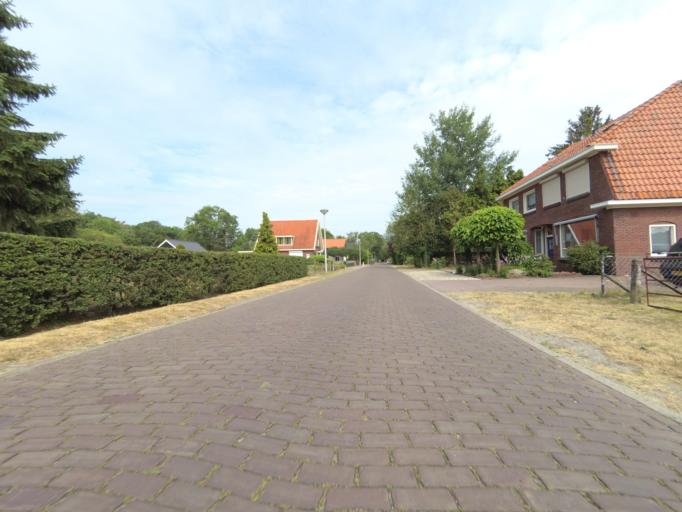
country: NL
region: Overijssel
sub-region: Gemeente Hengelo
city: Hengelo
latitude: 52.2084
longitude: 6.7947
